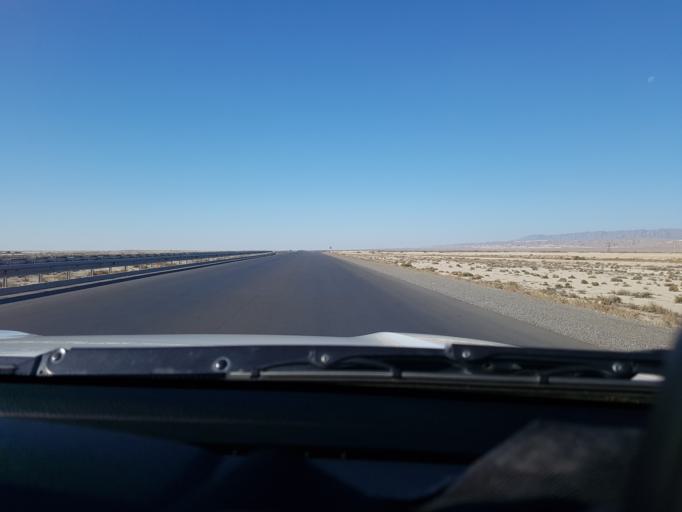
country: TM
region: Balkan
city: Gazanjyk
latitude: 39.2692
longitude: 55.1385
